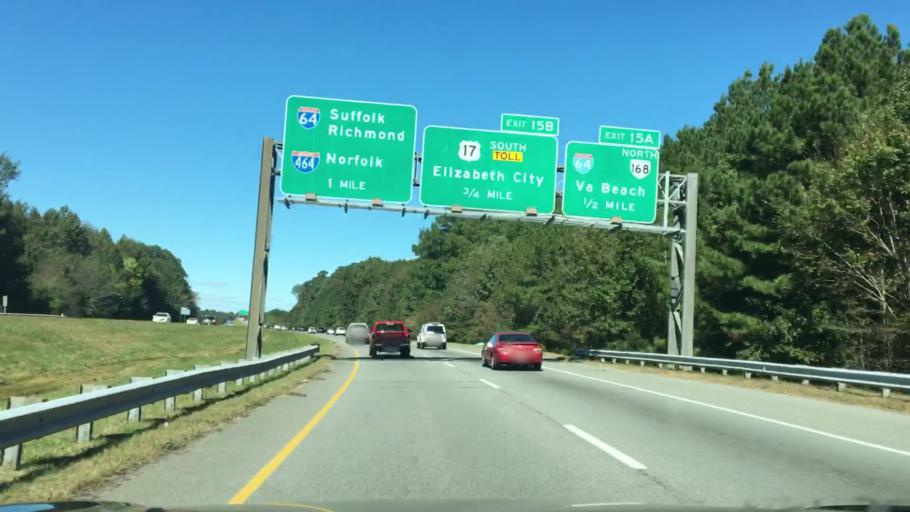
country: US
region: Virginia
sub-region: City of Chesapeake
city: Chesapeake
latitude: 36.7480
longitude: -76.2591
